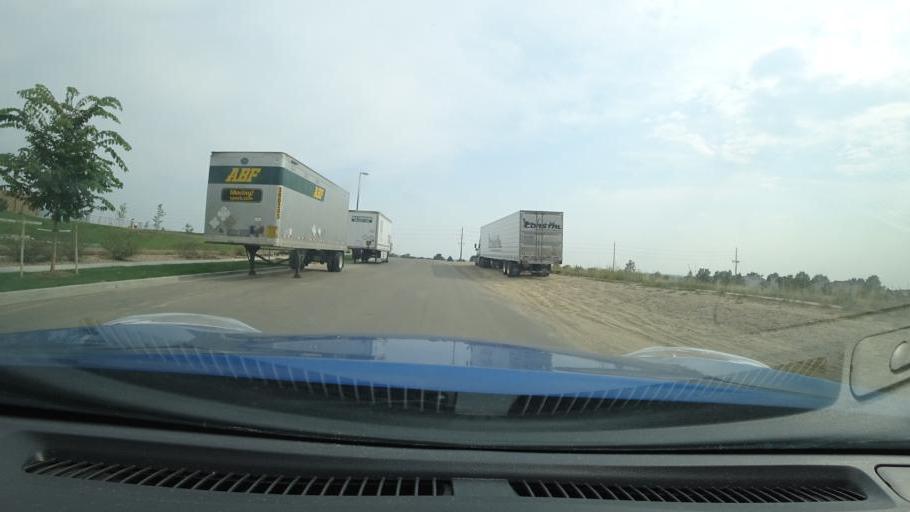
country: US
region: Colorado
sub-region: Adams County
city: Aurora
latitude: 39.7484
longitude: -104.7535
